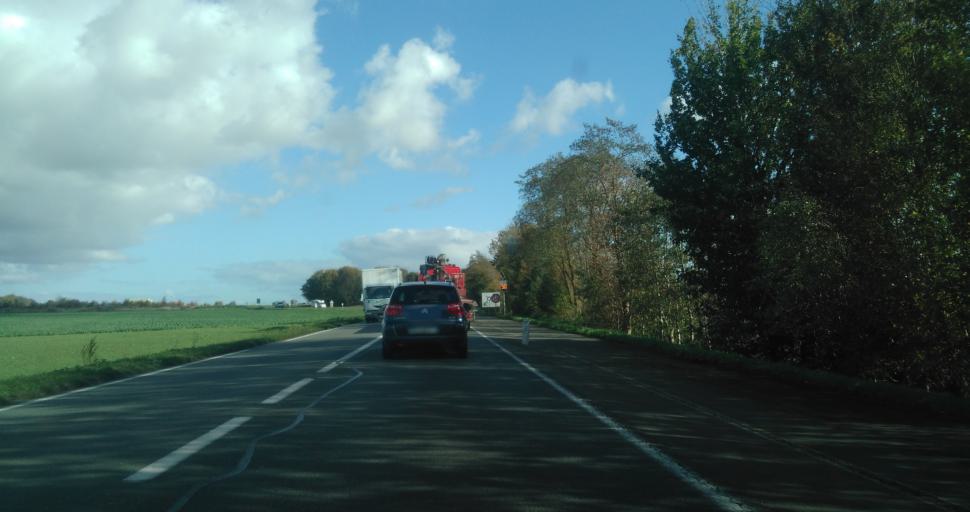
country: FR
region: Nord-Pas-de-Calais
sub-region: Departement du Pas-de-Calais
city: Anzin-Saint-Aubin
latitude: 50.3237
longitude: 2.7524
